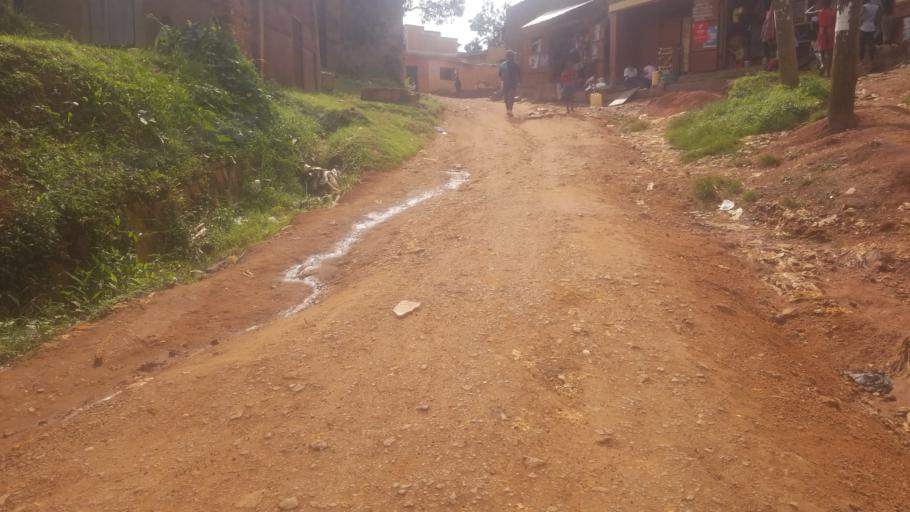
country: UG
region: Central Region
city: Kampala Central Division
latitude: 0.3302
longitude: 32.5592
